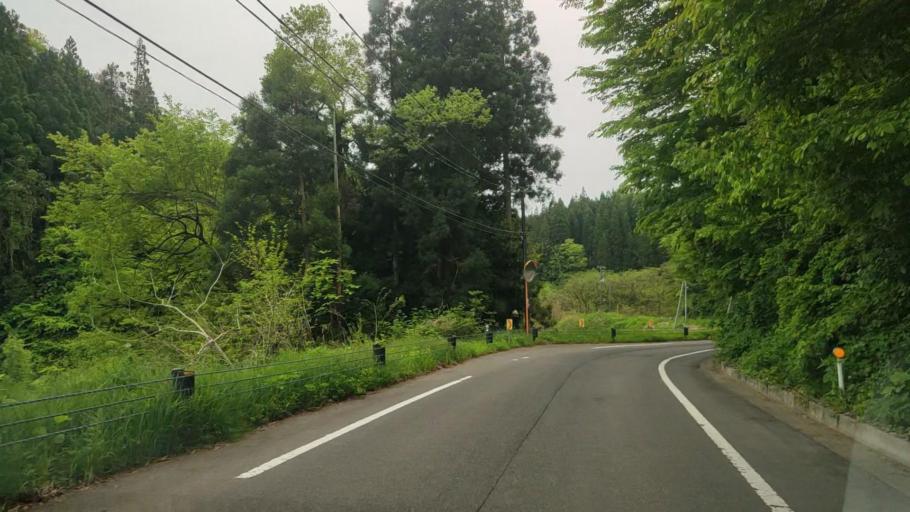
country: JP
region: Niigata
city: Gosen
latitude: 37.7154
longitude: 139.1240
